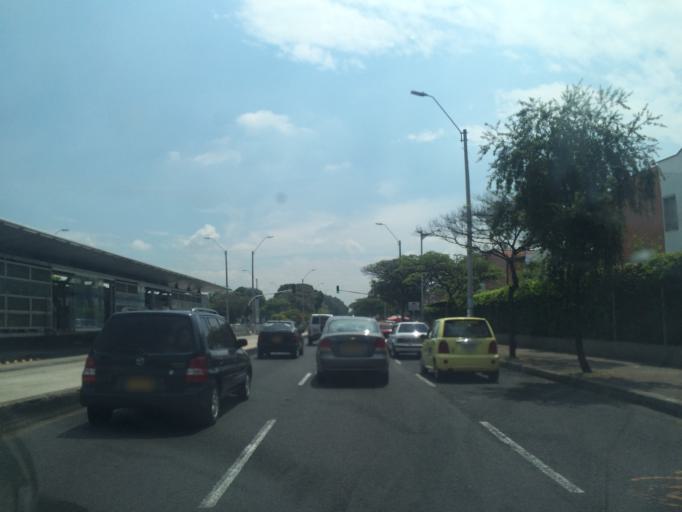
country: CO
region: Valle del Cauca
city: Cali
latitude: 3.4780
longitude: -76.5024
